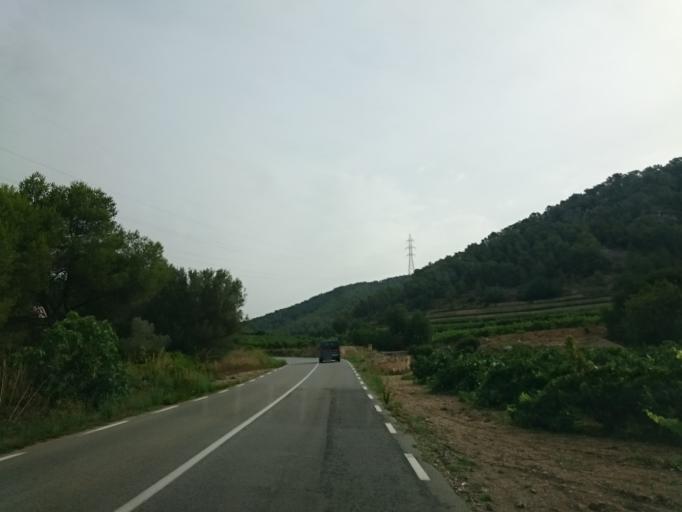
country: ES
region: Catalonia
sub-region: Provincia de Barcelona
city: Sant Pere de Ribes
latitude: 41.2742
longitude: 1.7880
